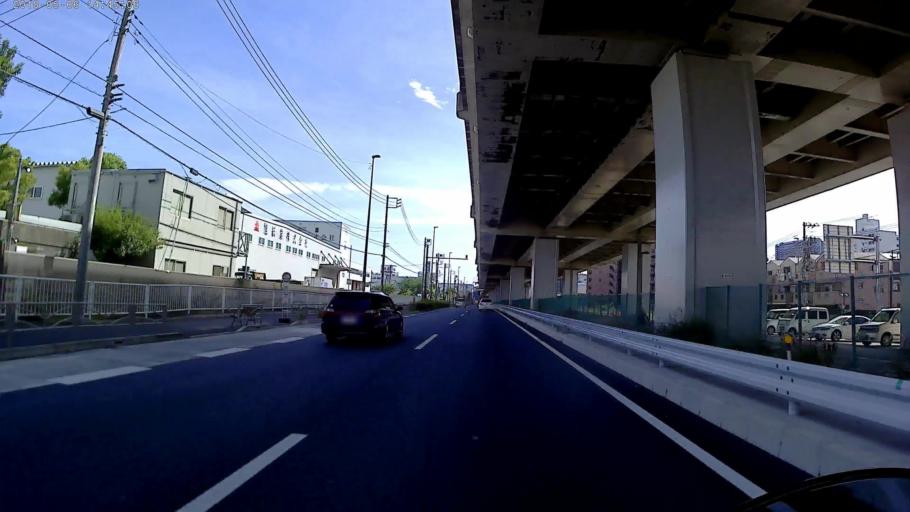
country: JP
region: Kanagawa
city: Yokohama
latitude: 35.4048
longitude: 139.6226
